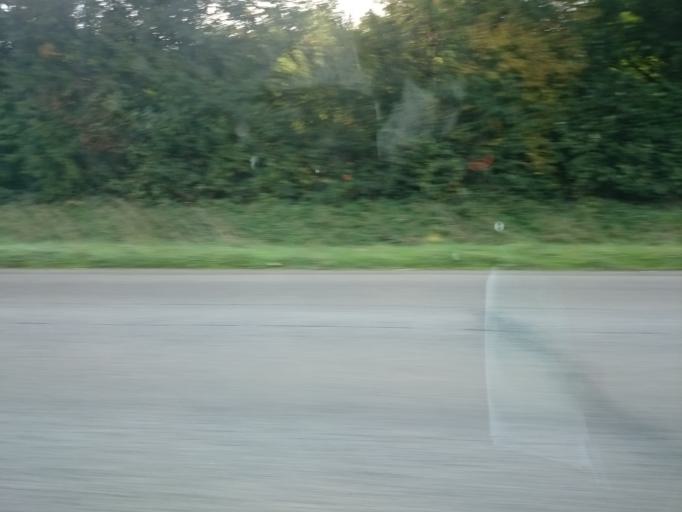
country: FR
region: Pays de la Loire
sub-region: Departement de la Loire-Atlantique
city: Heric
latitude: 47.4471
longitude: -1.6414
